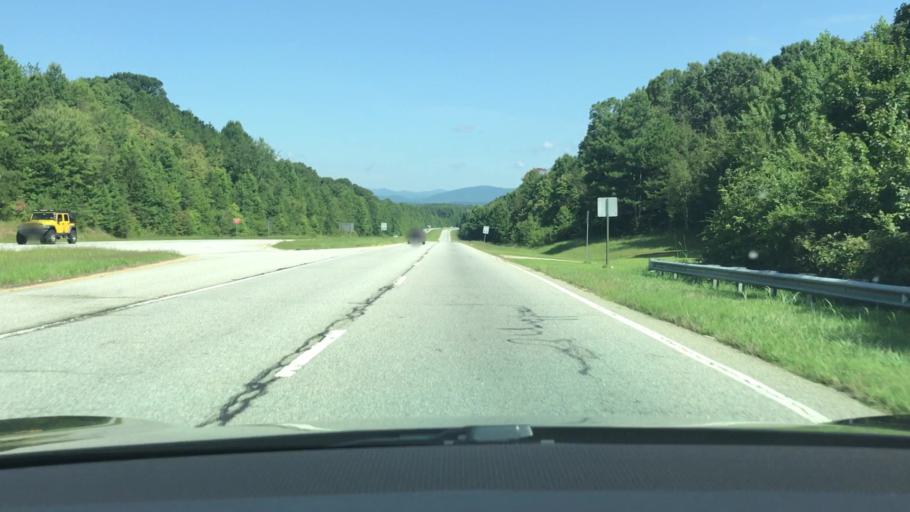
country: US
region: Georgia
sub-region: Habersham County
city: Clarkesville
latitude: 34.5987
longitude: -83.4424
